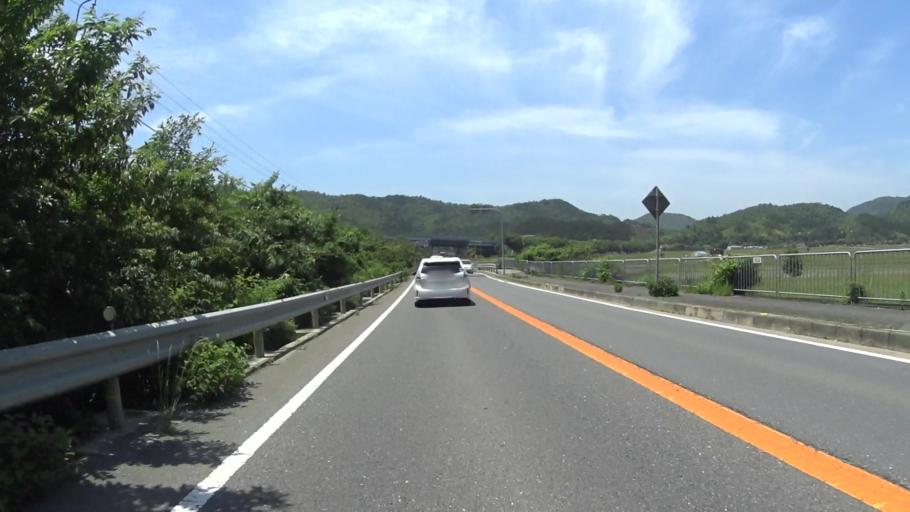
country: JP
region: Kyoto
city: Kameoka
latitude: 35.0818
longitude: 135.5136
